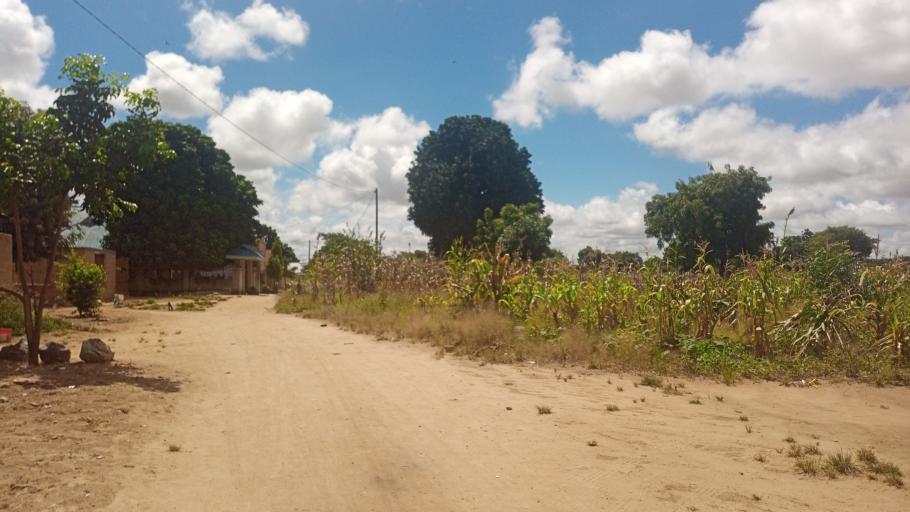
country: TZ
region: Dodoma
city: Kisasa
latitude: -6.1783
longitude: 35.7668
